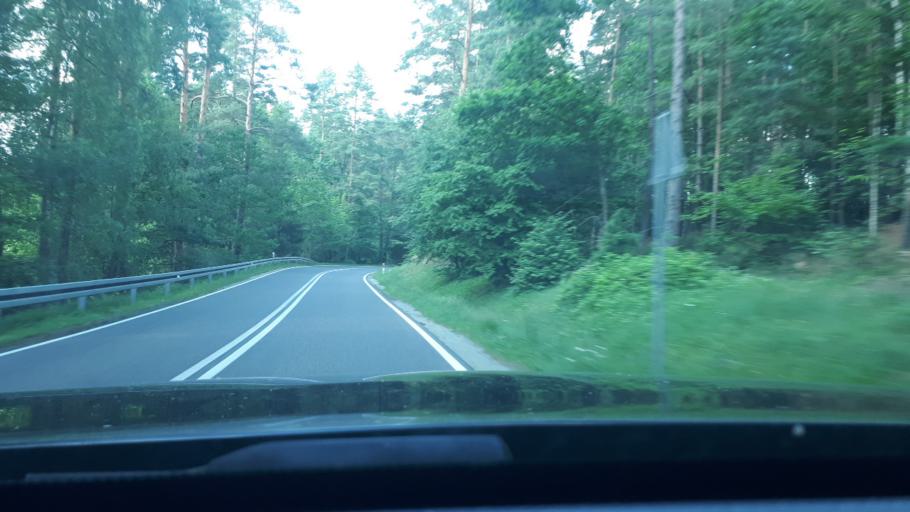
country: PL
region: Warmian-Masurian Voivodeship
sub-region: Powiat olsztynski
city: Stawiguda
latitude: 53.5344
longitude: 20.4614
